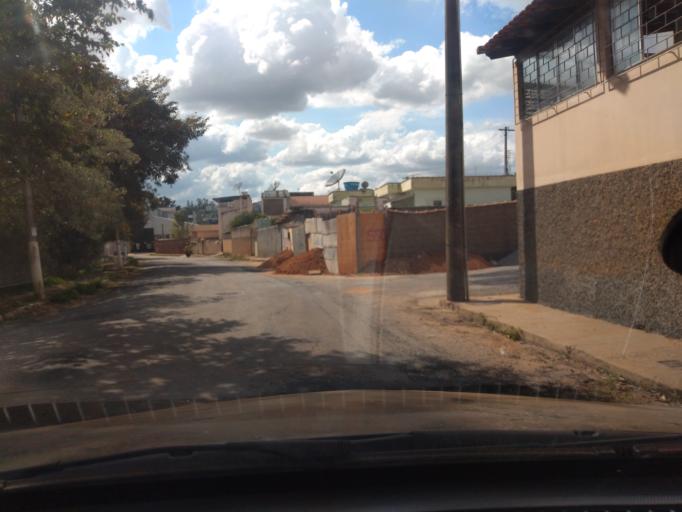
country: BR
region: Minas Gerais
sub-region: Tres Coracoes
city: Tres Coracoes
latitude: -21.7055
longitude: -45.2535
